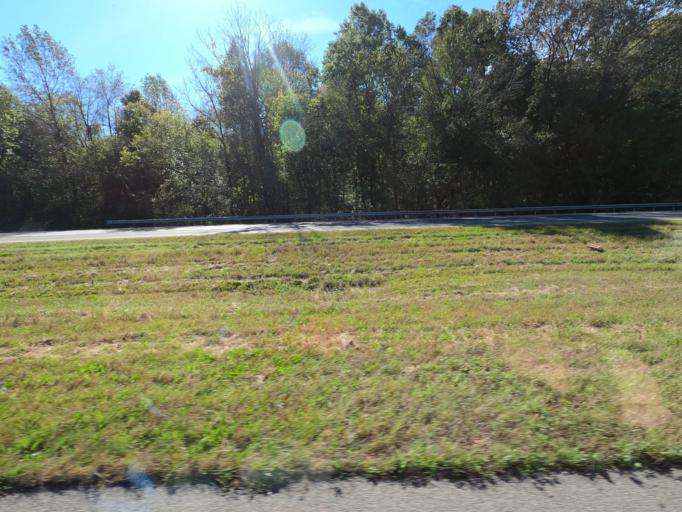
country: US
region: Tennessee
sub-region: Dickson County
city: Burns
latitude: 36.0188
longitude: -87.2386
